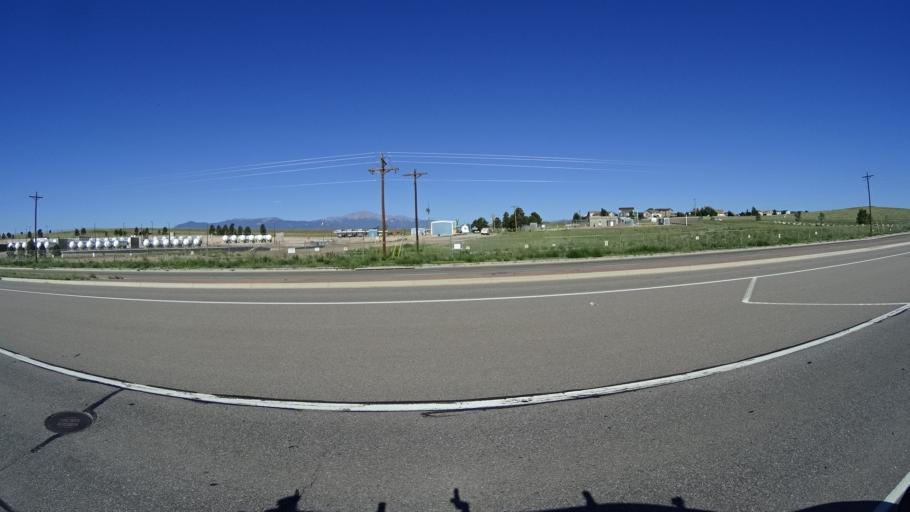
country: US
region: Colorado
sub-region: El Paso County
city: Cimarron Hills
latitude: 38.8857
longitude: -104.6826
